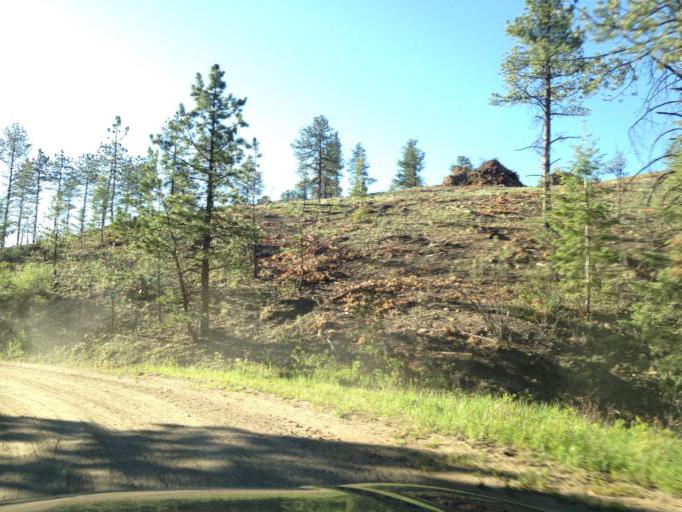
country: US
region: Colorado
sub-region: Jefferson County
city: Evergreen
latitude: 39.4032
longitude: -105.4963
